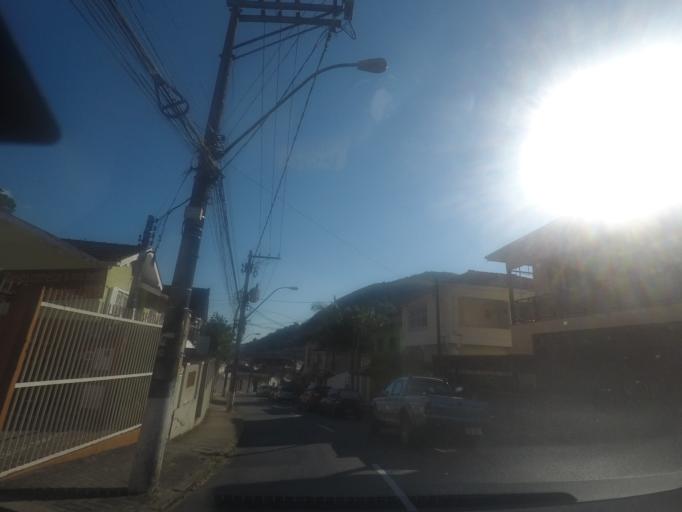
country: BR
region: Rio de Janeiro
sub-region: Petropolis
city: Petropolis
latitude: -22.5148
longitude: -43.1679
